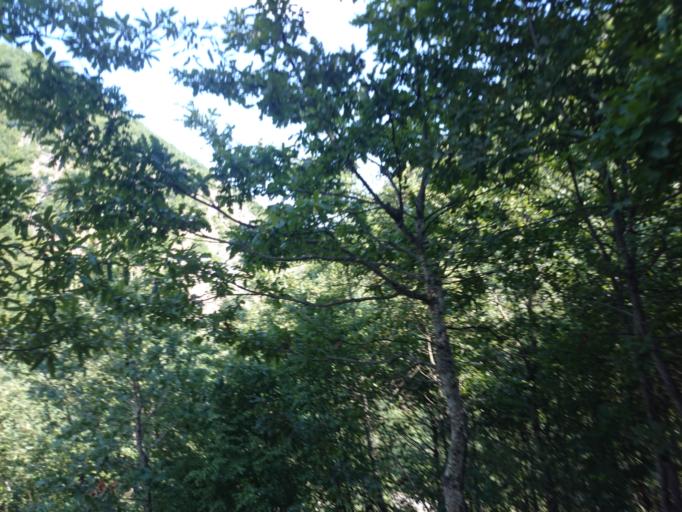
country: AL
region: Diber
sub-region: Rrethi i Dibres
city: Arras
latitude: 41.7418
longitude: 20.2840
